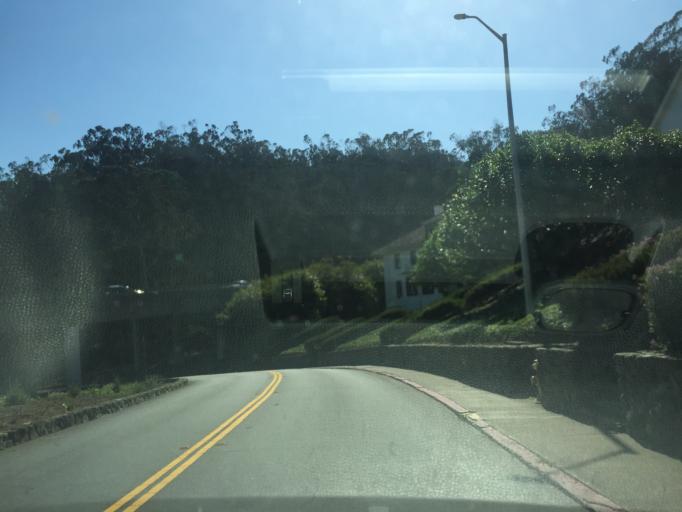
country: US
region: California
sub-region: San Francisco County
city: San Francisco
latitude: 37.7983
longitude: -122.4701
